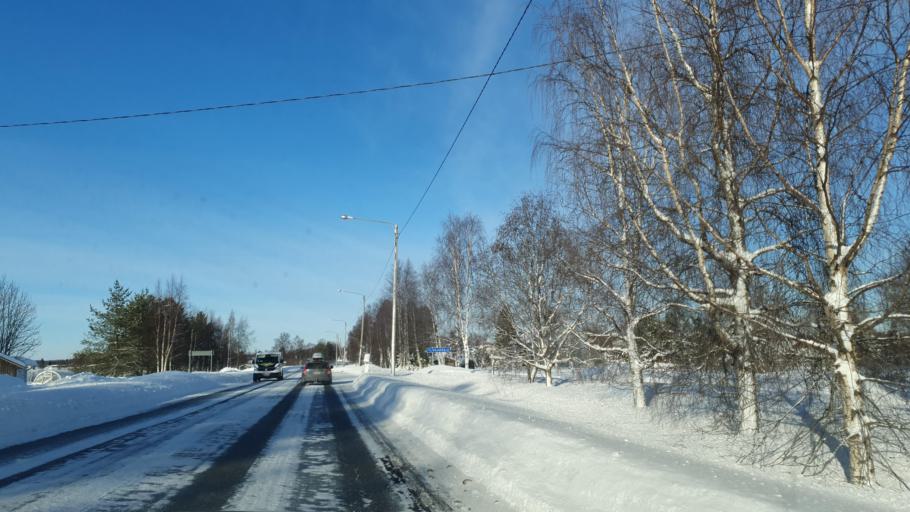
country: FI
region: Lapland
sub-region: Kemi-Tornio
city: Tornio
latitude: 65.9273
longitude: 24.1282
